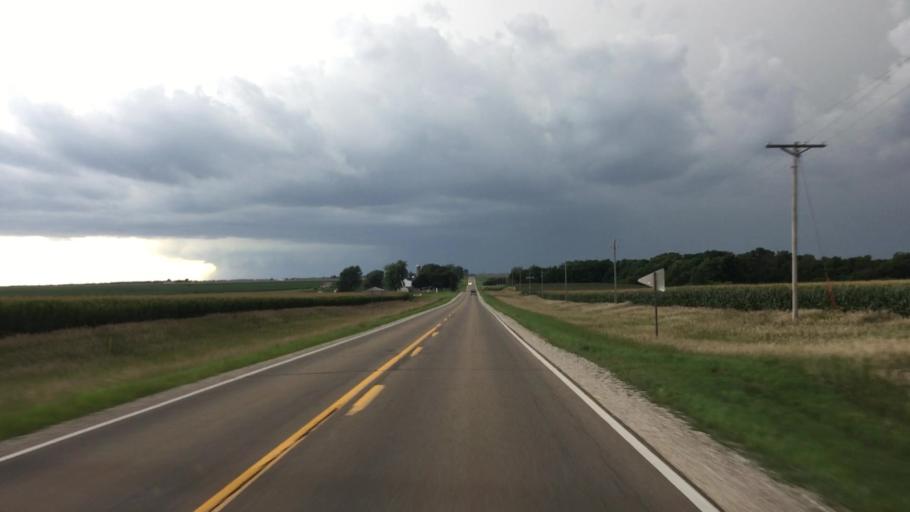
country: US
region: Iowa
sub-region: Henry County
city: New London
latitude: 40.7733
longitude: -91.4502
